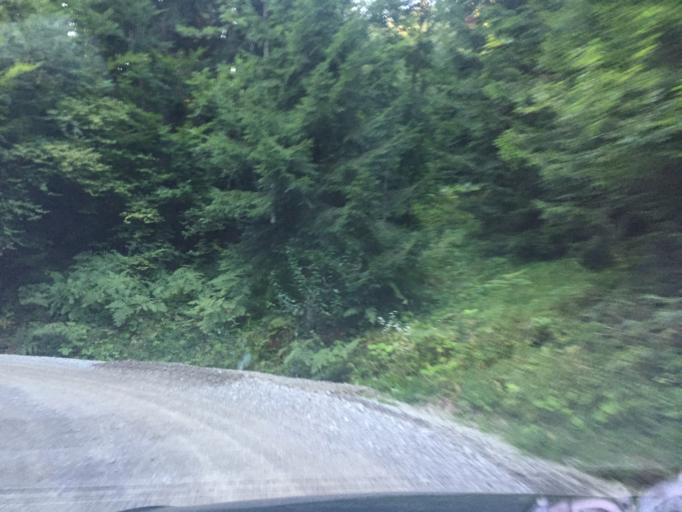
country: SI
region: Sostanj
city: Topolsica
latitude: 46.4549
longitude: 14.9837
